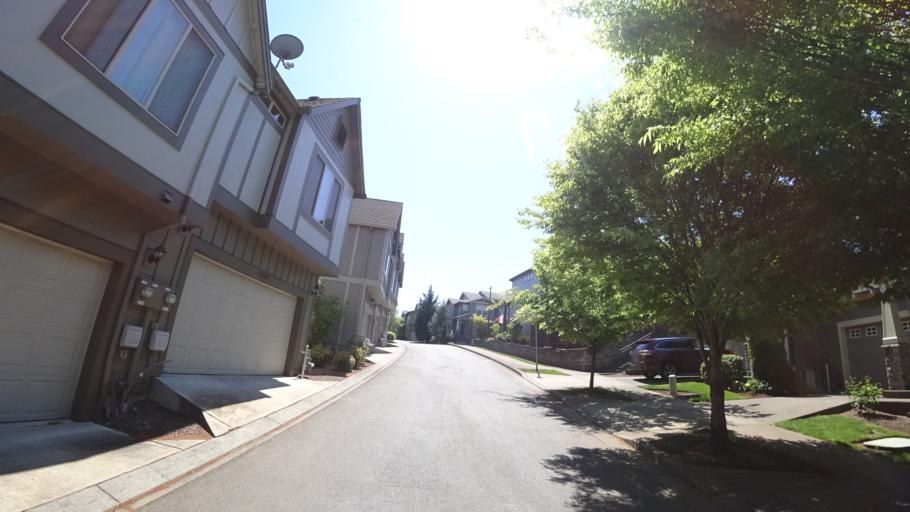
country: US
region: Oregon
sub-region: Washington County
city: King City
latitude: 45.4341
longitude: -122.8323
